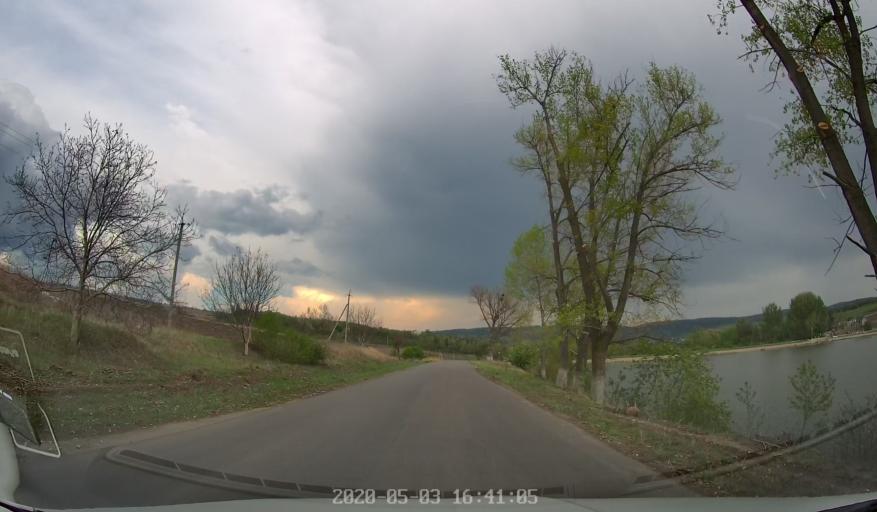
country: MD
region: Stinga Nistrului
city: Bucovat
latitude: 47.1698
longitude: 28.4025
